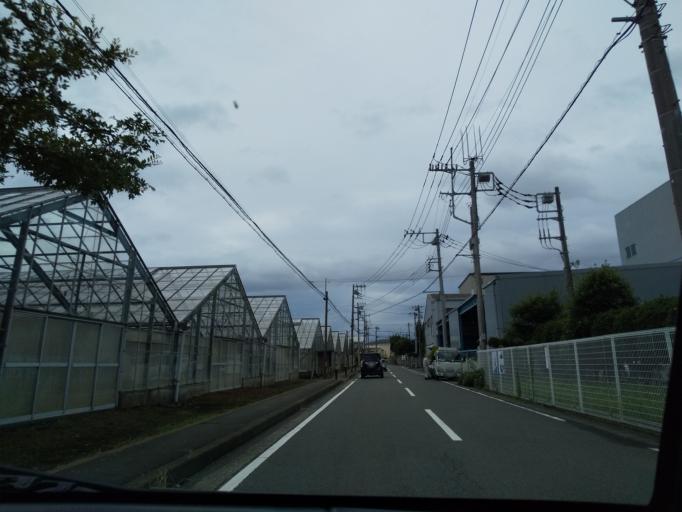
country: JP
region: Kanagawa
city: Minami-rinkan
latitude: 35.4389
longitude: 139.4399
